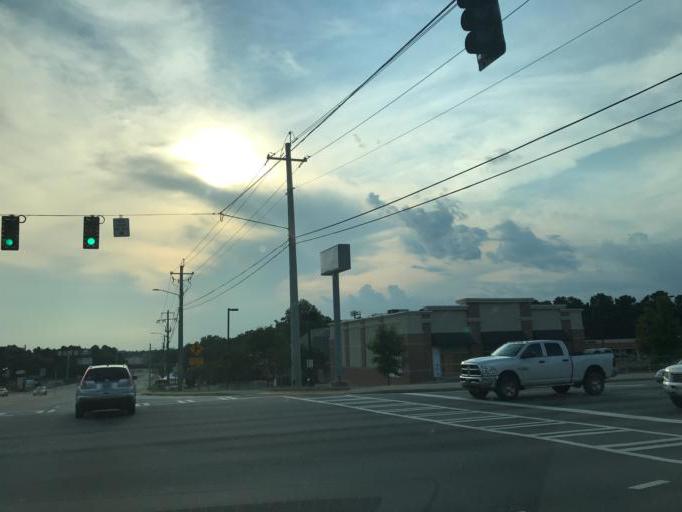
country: US
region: Alabama
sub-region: Russell County
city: Phenix City
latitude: 32.5396
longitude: -84.9542
